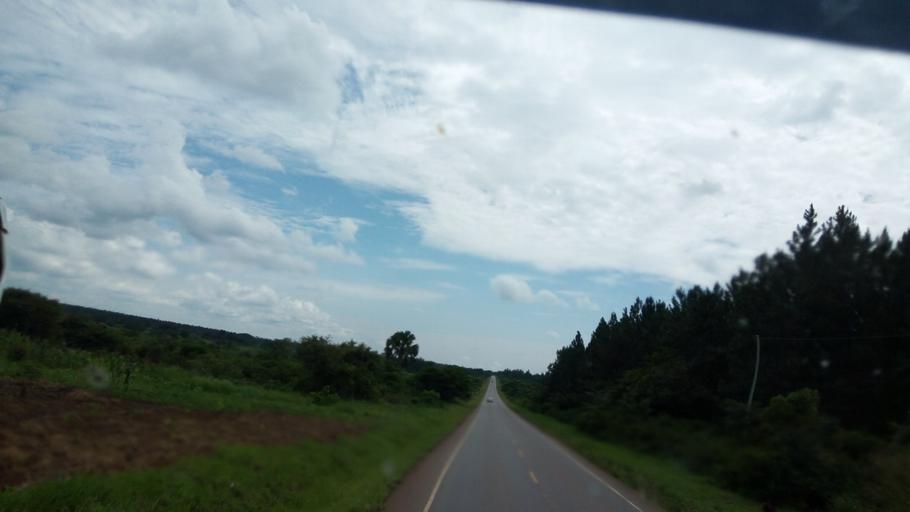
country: UG
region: Central Region
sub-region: Nakasongola District
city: Nakasongola
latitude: 1.2029
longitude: 32.4629
